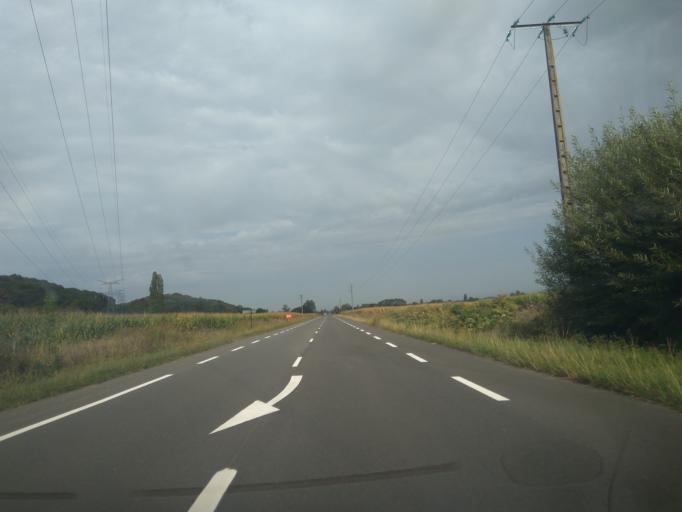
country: FR
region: Aquitaine
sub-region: Departement des Pyrenees-Atlantiques
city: Arbus
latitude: 43.3413
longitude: -0.5121
